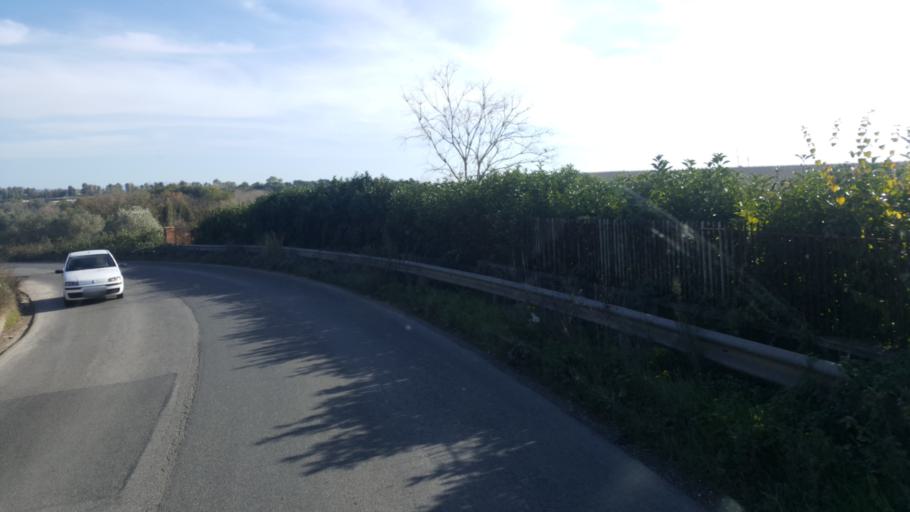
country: IT
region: Latium
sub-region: Citta metropolitana di Roma Capitale
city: Mantiglia di Ardea
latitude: 41.6891
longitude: 12.6009
